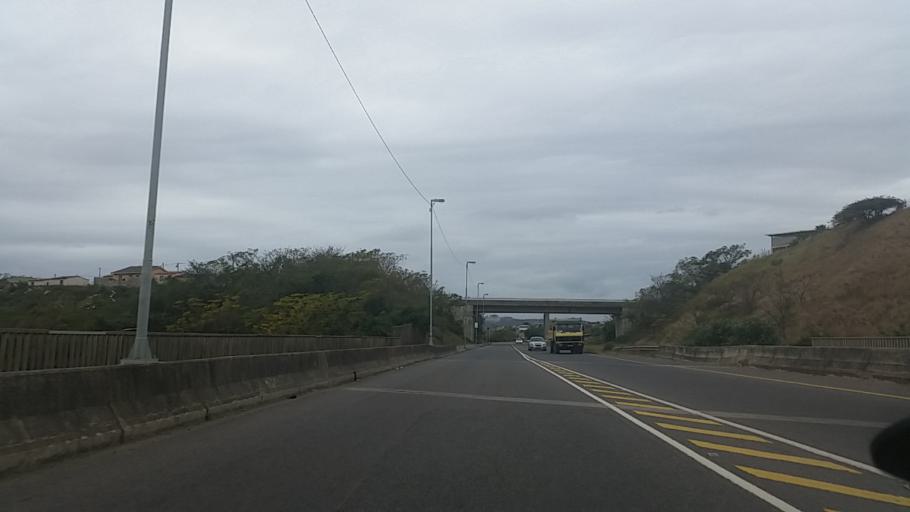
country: ZA
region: KwaZulu-Natal
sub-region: eThekwini Metropolitan Municipality
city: Berea
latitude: -29.8579
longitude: 30.9401
